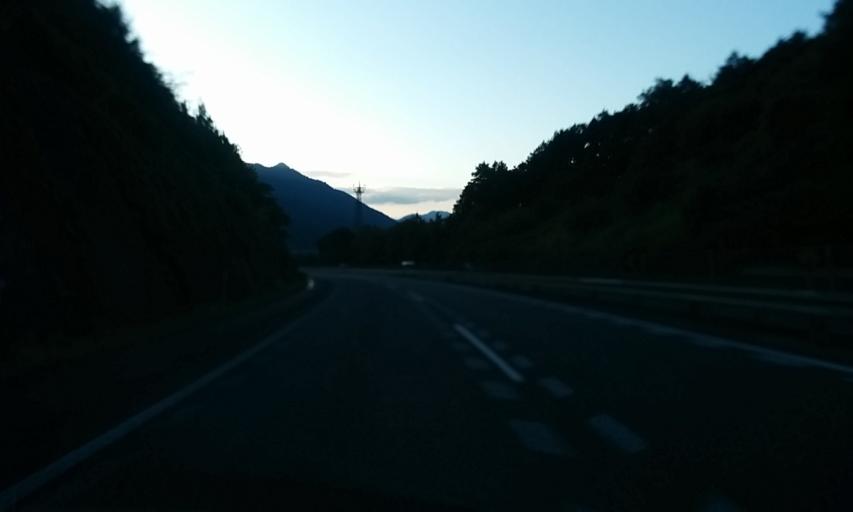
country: JP
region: Hyogo
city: Sasayama
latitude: 35.1400
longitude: 135.1361
